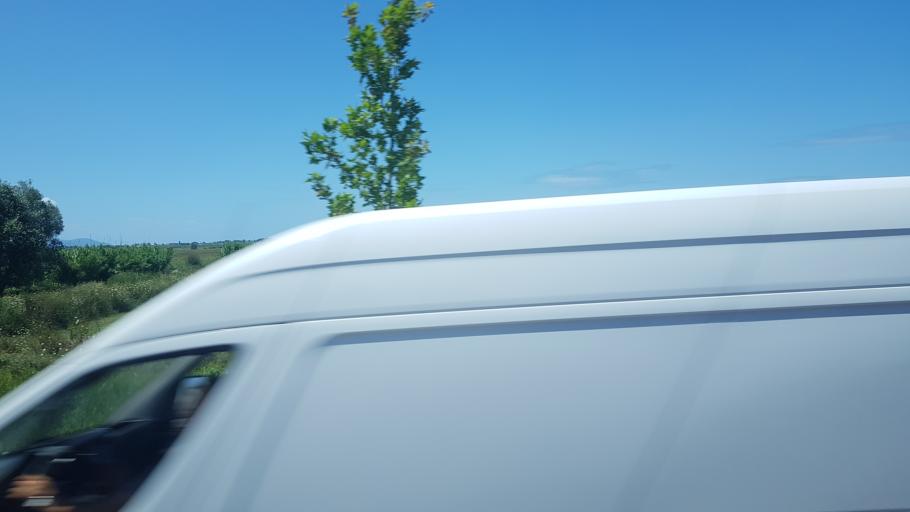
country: AL
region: Fier
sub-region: Rrethi i Fierit
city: Frakulla e Madhe
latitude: 40.6595
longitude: 19.4898
